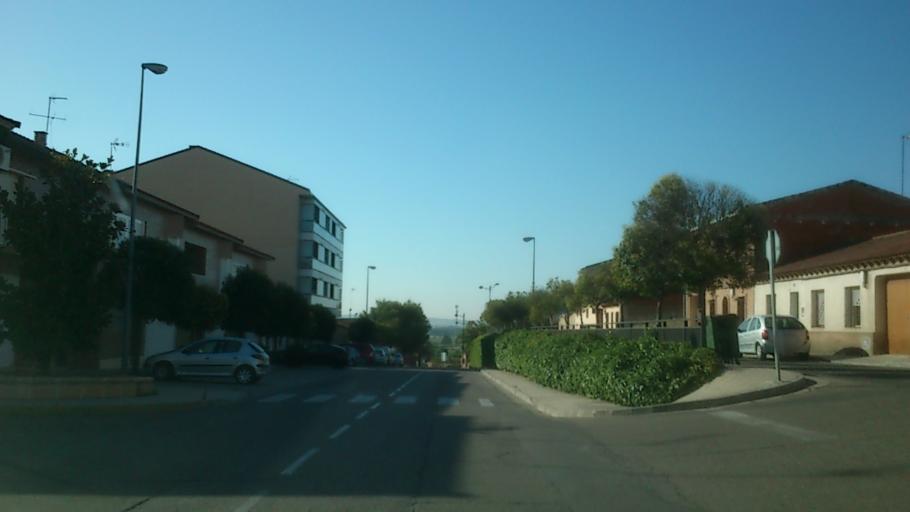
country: ES
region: Aragon
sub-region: Provincia de Zaragoza
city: Villanueva de Gallego
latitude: 41.7725
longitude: -0.8237
